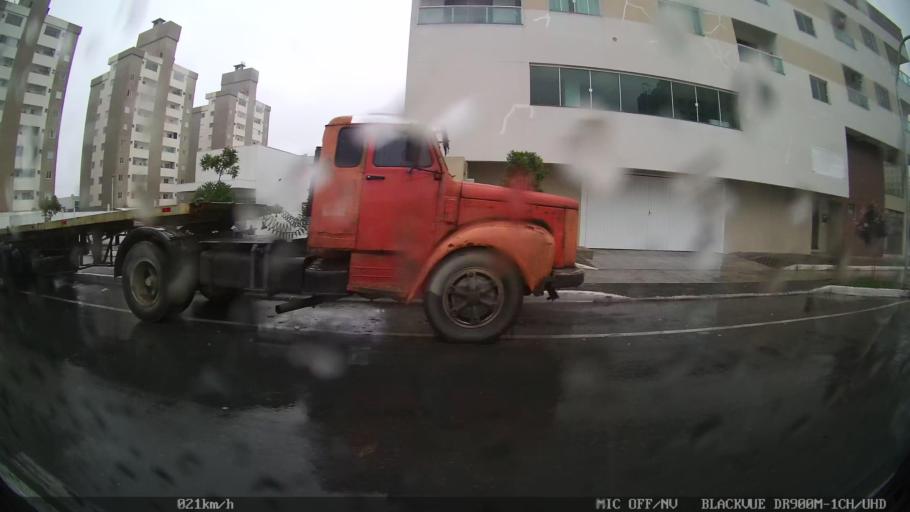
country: BR
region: Santa Catarina
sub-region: Itajai
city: Itajai
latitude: -26.9099
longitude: -48.6808
